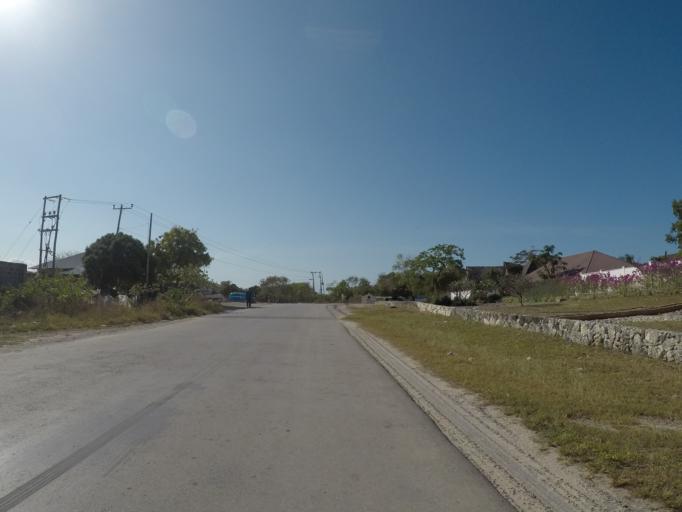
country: TZ
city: Kiwengwa
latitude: -6.1430
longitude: 39.5134
